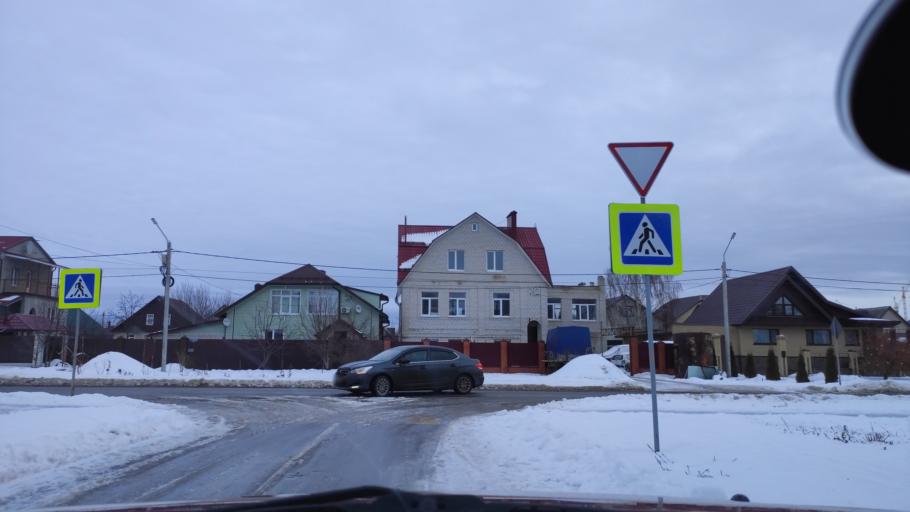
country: RU
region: Tambov
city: Tambov
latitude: 52.7630
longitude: 41.3754
